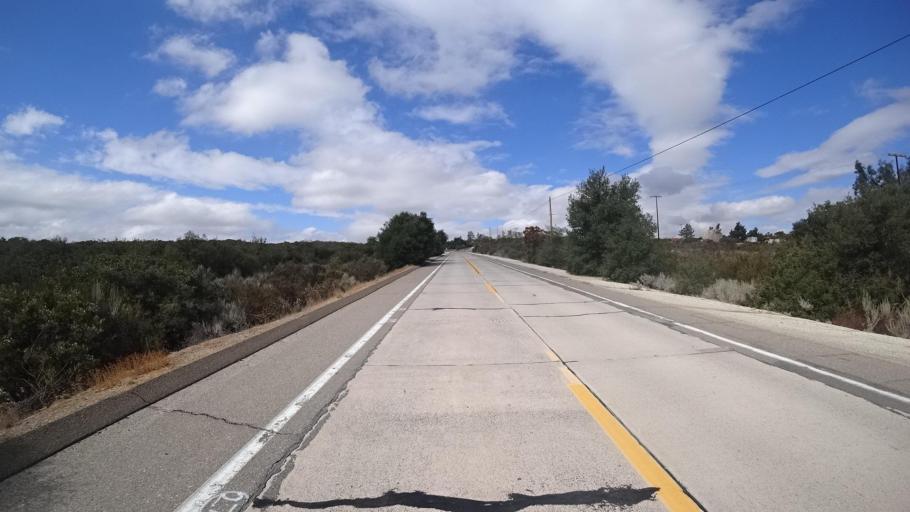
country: US
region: California
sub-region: San Diego County
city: Campo
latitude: 32.6691
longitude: -116.3063
